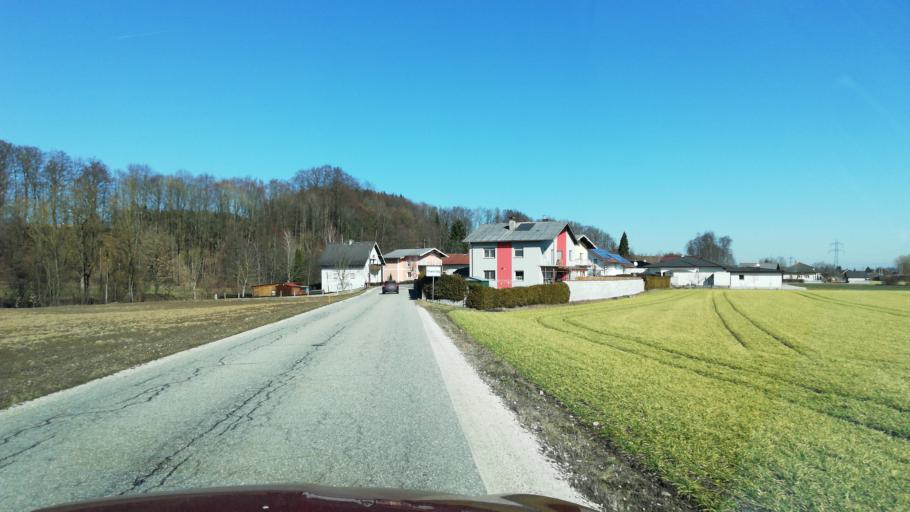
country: AT
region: Upper Austria
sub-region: Politischer Bezirk Vocklabruck
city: Redlham
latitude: 48.0317
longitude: 13.7369
